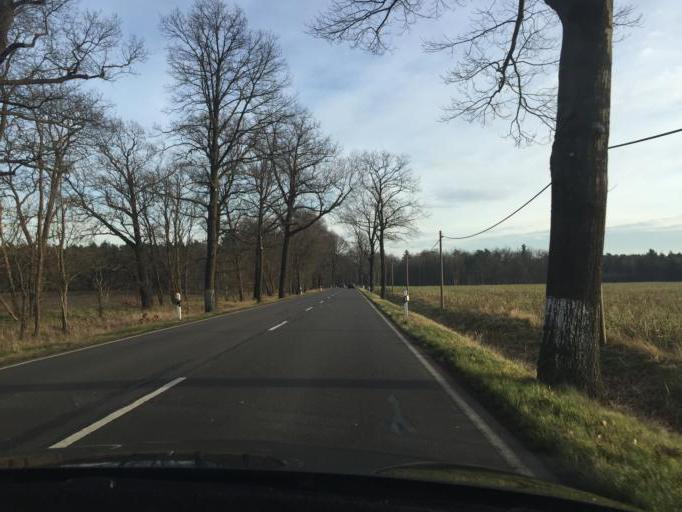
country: DE
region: Brandenburg
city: Cottbus
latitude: 51.7448
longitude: 14.3860
